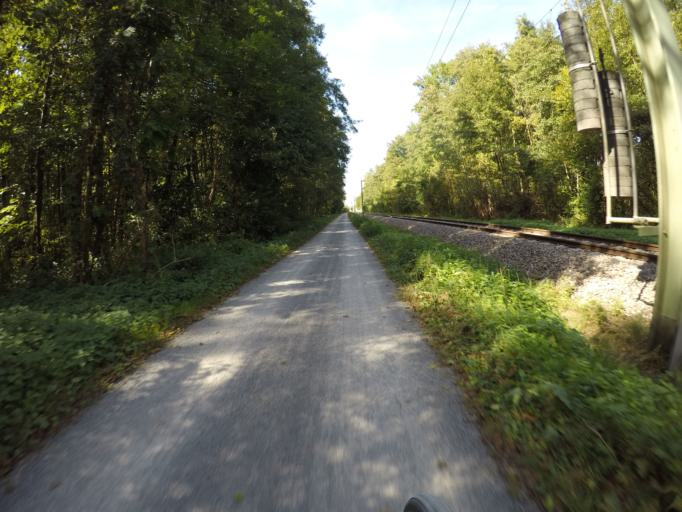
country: DE
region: Baden-Wuerttemberg
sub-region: Karlsruhe Region
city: Zaisenhausen
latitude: 49.1186
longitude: 8.7321
